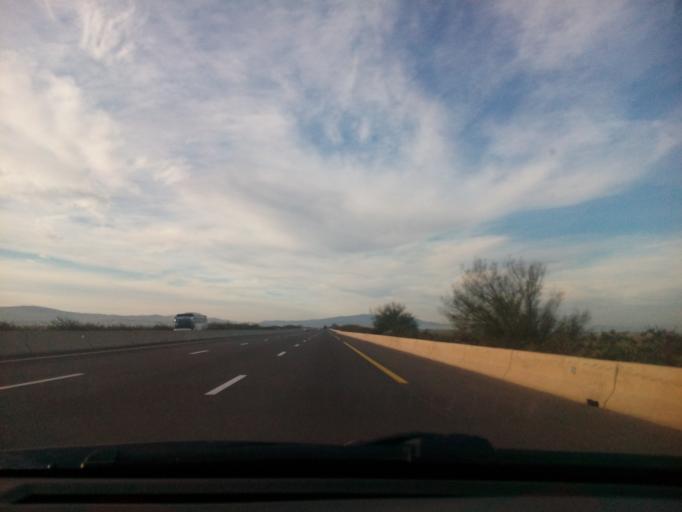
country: DZ
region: Mascara
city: Mascara
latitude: 35.6663
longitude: 0.1403
